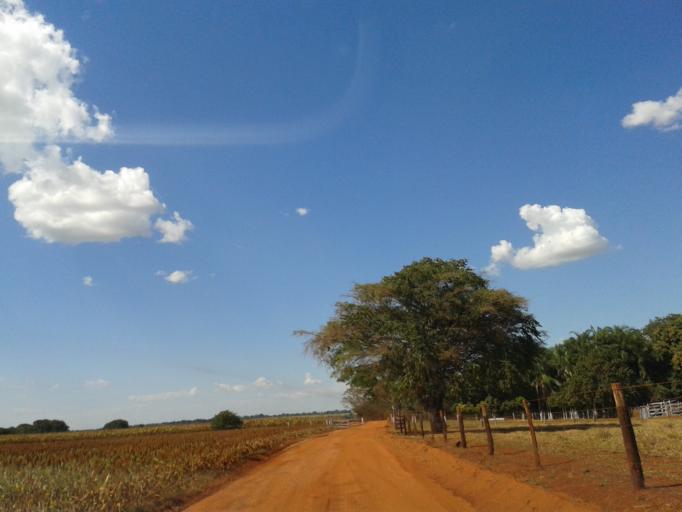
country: BR
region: Minas Gerais
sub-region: Capinopolis
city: Capinopolis
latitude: -18.6014
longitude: -49.5074
